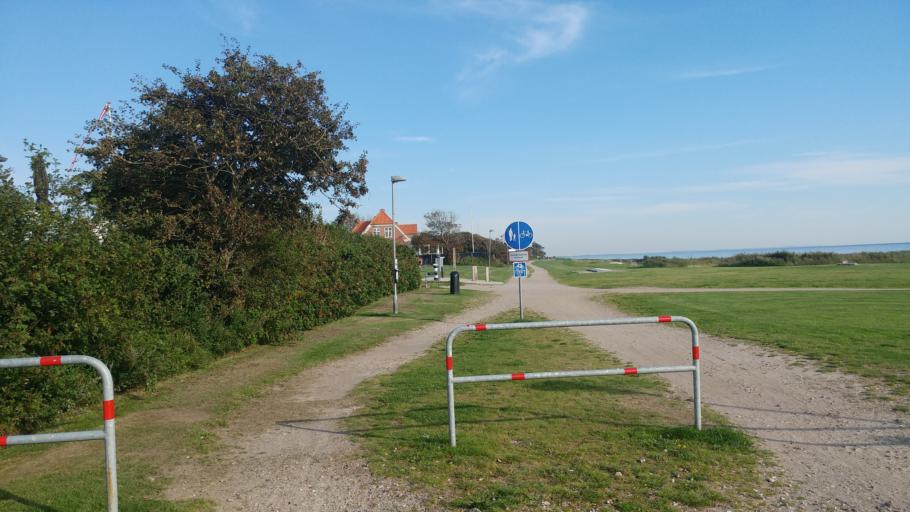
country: DK
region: Central Jutland
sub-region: Ringkobing-Skjern Kommune
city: Ringkobing
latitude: 56.0867
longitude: 8.2442
